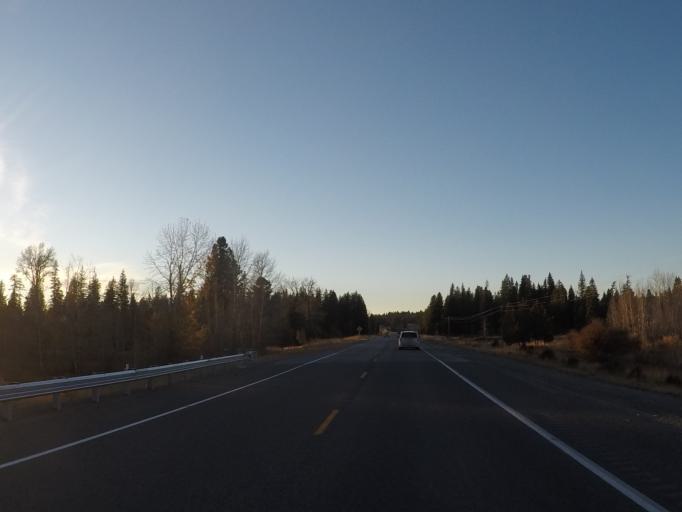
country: US
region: Montana
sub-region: Lewis and Clark County
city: Lincoln
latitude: 47.0006
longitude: -113.0369
